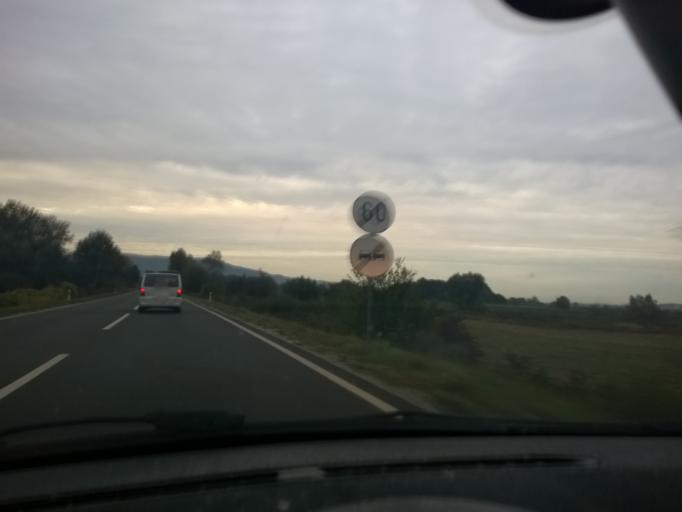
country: HR
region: Zagrebacka
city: Pojatno
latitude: 45.9288
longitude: 15.8207
